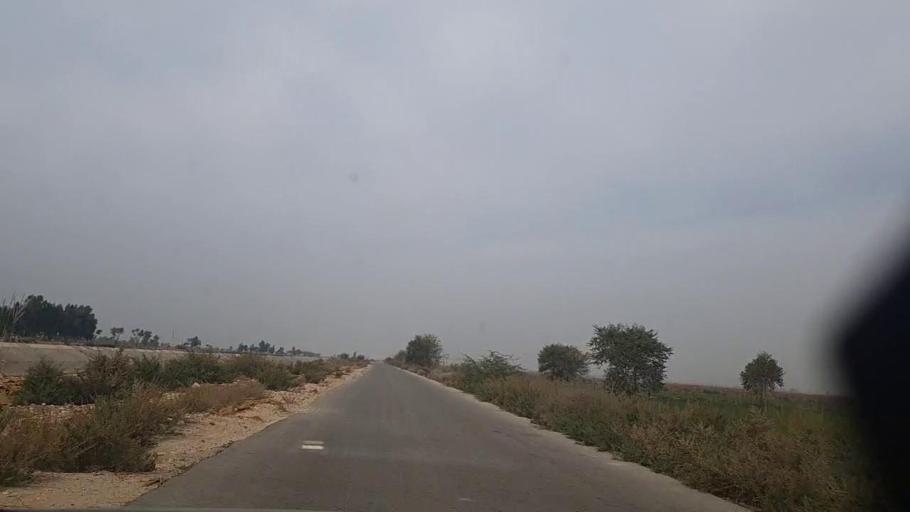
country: PK
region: Sindh
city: Sakrand
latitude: 26.2575
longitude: 68.2454
